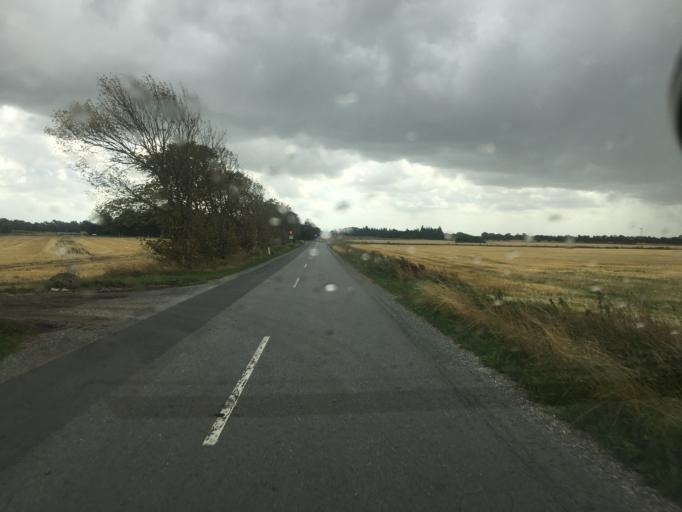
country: DK
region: South Denmark
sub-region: Tonder Kommune
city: Logumkloster
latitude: 54.9923
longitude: 8.9625
